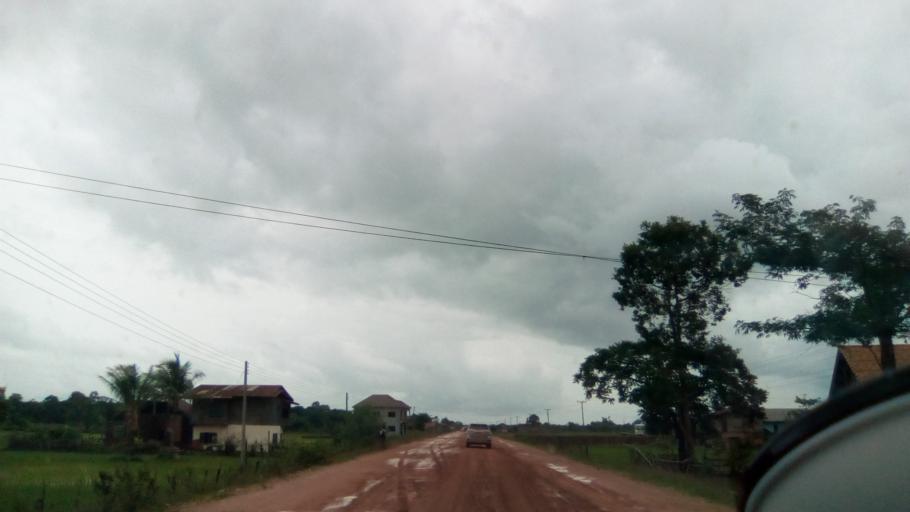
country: LA
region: Attapu
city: Attapu
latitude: 14.7388
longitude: 106.6886
